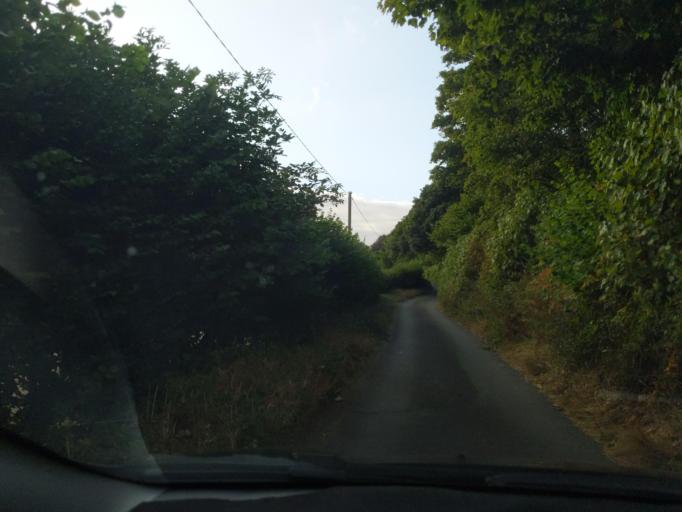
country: GB
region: England
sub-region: Devon
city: Salcombe
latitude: 50.2291
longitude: -3.7938
